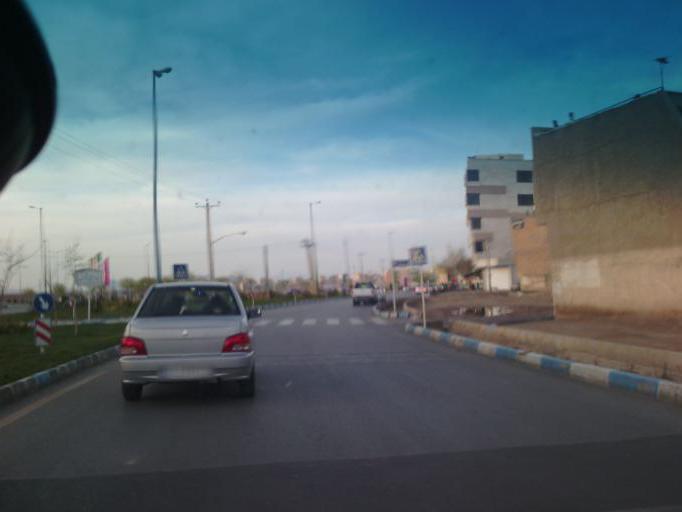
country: IR
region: Isfahan
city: Shahin Shahr
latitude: 32.8676
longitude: 51.5407
